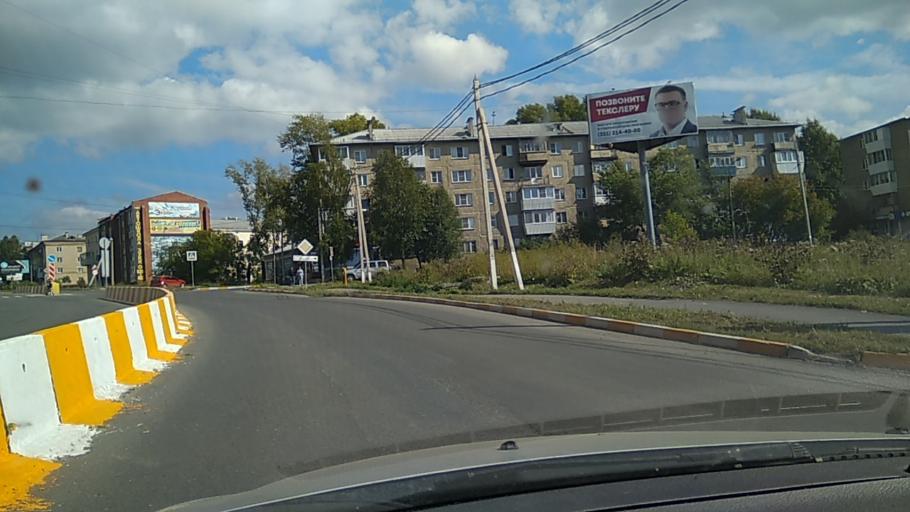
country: RU
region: Chelyabinsk
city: Zlatoust
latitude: 55.1137
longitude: 59.7118
